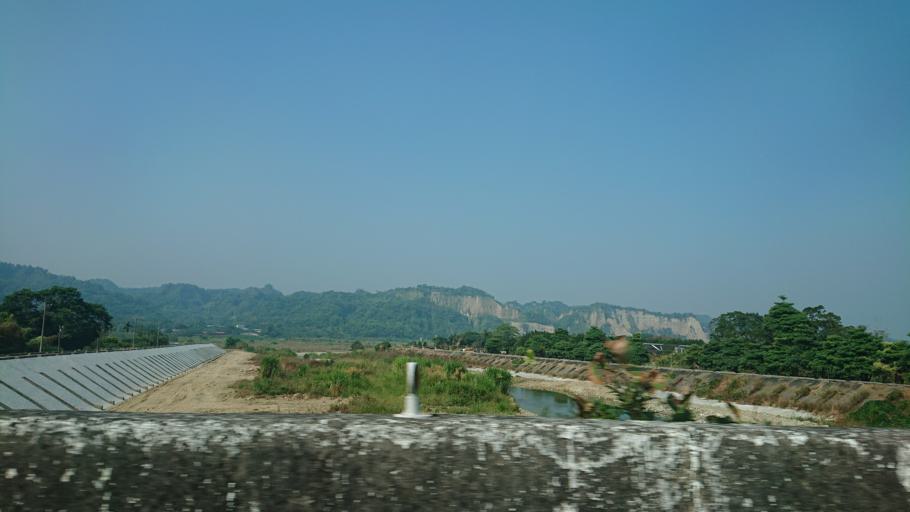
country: TW
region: Taiwan
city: Lugu
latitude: 23.7295
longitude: 120.6669
